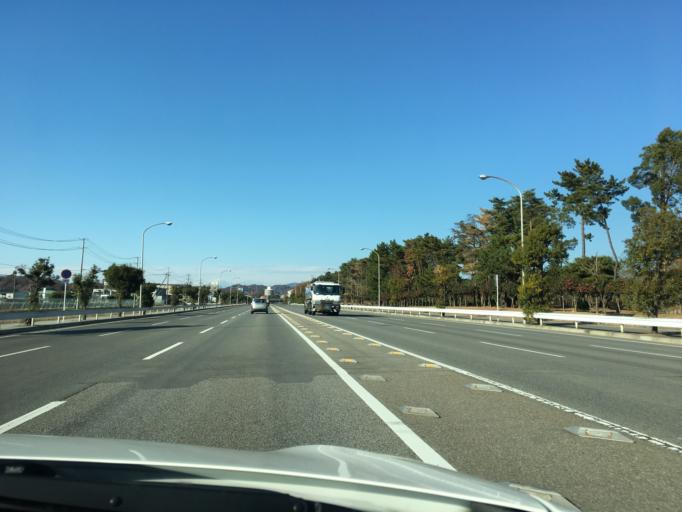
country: JP
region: Fukushima
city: Iwaki
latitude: 36.9332
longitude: 140.8604
